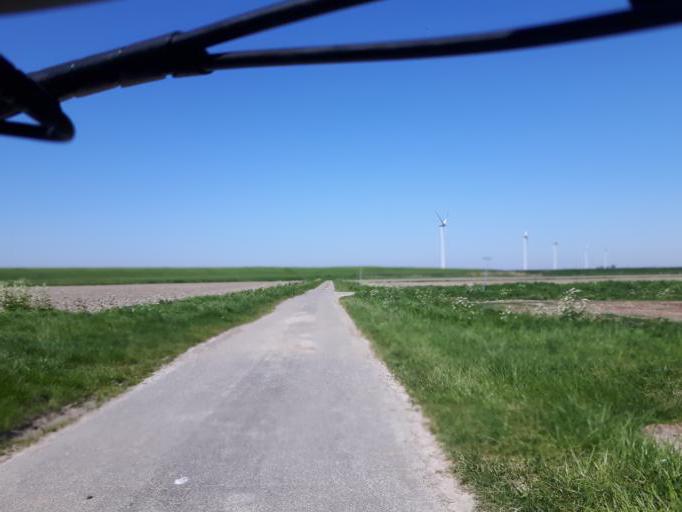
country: NL
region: Zeeland
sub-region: Gemeente Reimerswaal
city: Yerseke
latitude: 51.5502
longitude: 4.0547
